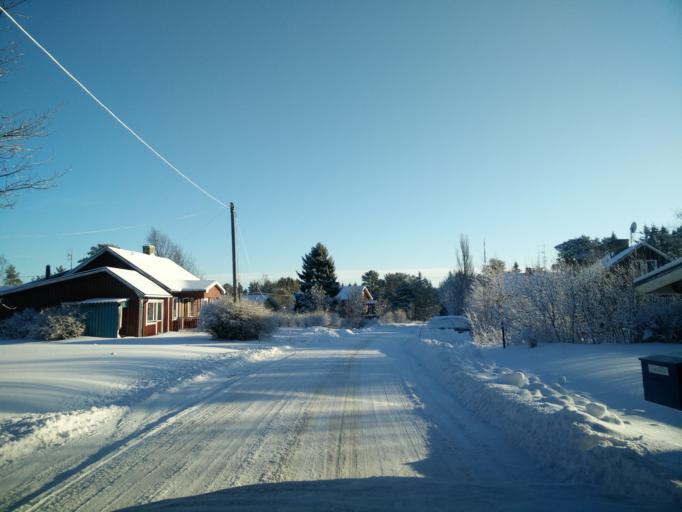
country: SE
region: Vaesternorrland
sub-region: Sundsvalls Kommun
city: Njurundabommen
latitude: 62.2337
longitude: 17.6526
